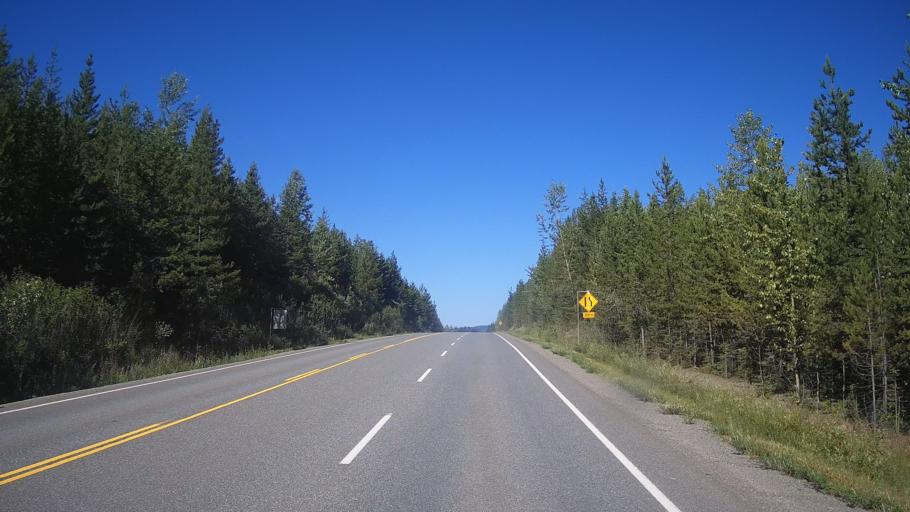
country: CA
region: British Columbia
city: Kamloops
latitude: 51.4975
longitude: -120.3739
